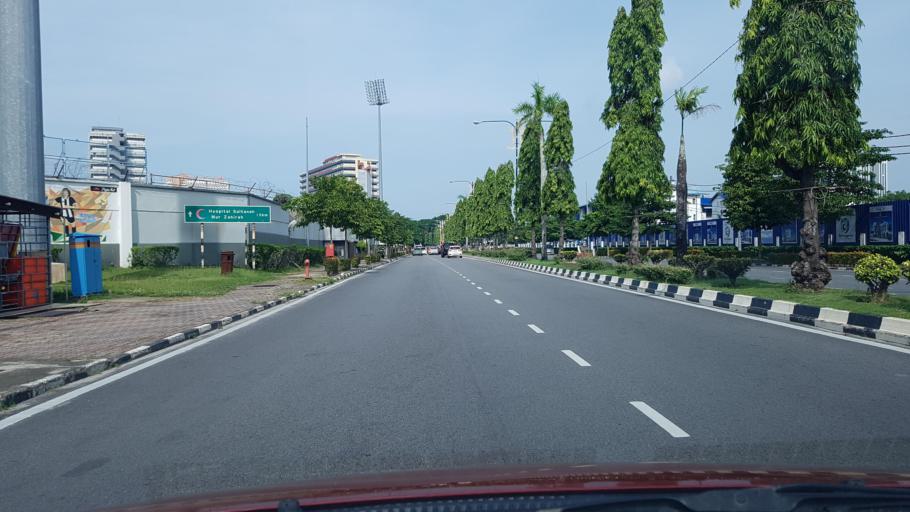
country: MY
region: Terengganu
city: Kuala Terengganu
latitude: 5.3291
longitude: 103.1391
